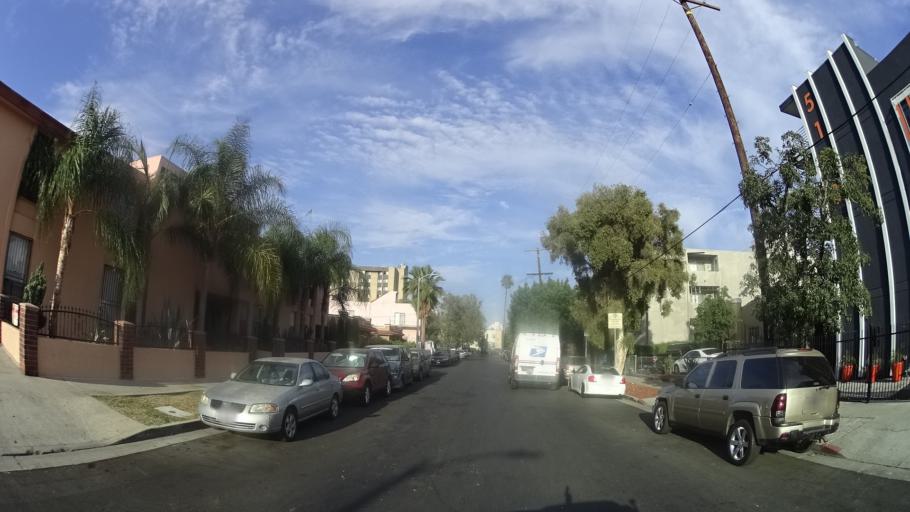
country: US
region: California
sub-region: Los Angeles County
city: Hollywood
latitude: 34.0967
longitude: -118.3018
